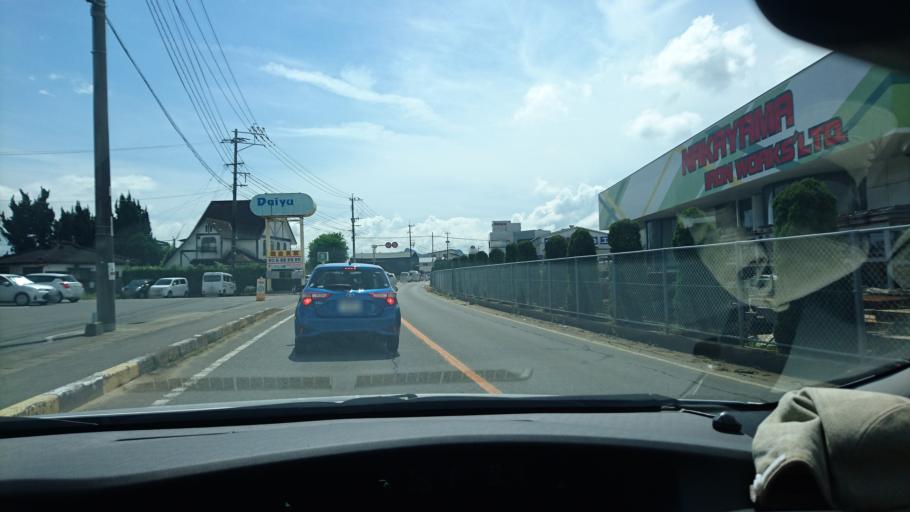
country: JP
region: Saga Prefecture
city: Takeocho-takeo
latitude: 33.2118
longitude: 130.0472
